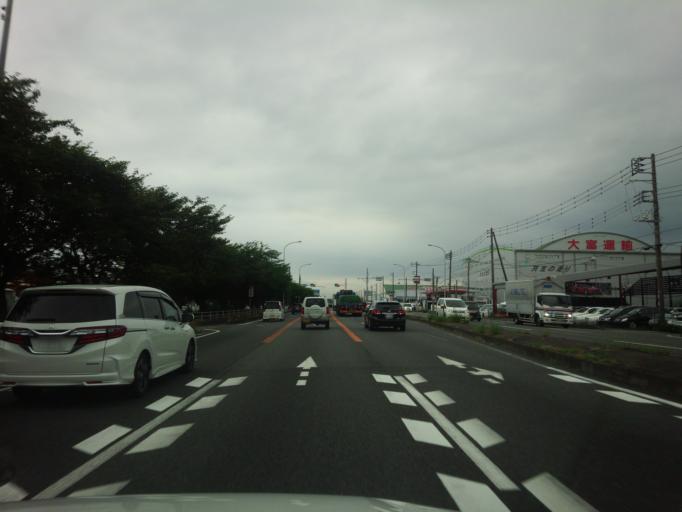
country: JP
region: Shizuoka
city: Numazu
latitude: 35.1170
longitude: 138.8338
